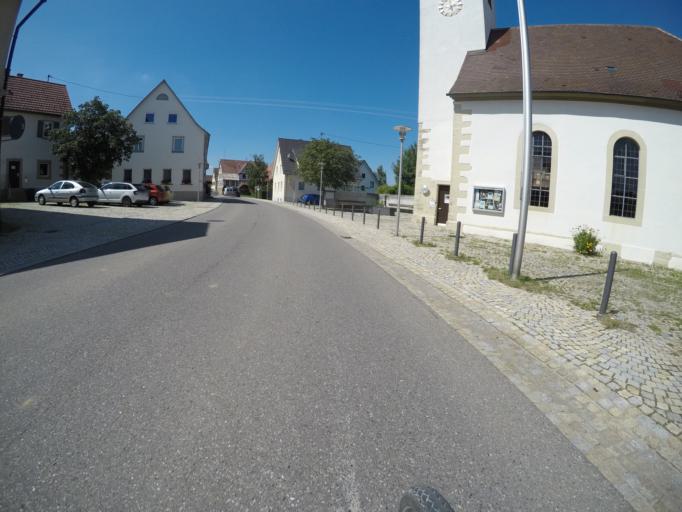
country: DE
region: Baden-Wuerttemberg
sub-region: Regierungsbezirk Stuttgart
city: Herrenberg
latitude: 48.5829
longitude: 8.8402
